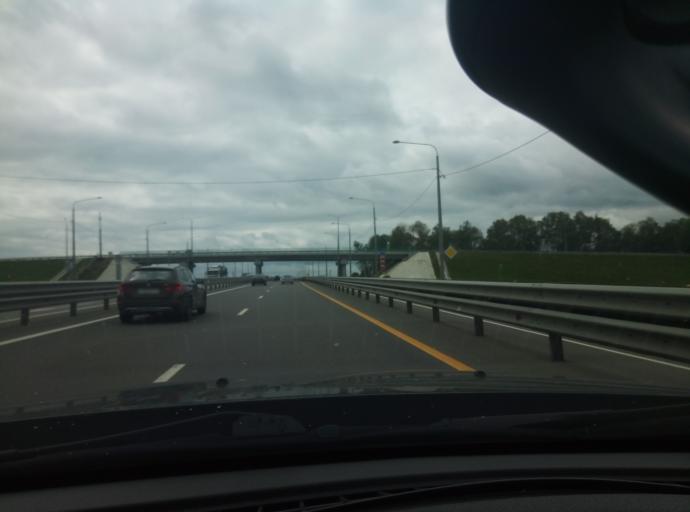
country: RU
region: Kaluga
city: Maloyaroslavets
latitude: 54.9575
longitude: 36.4576
